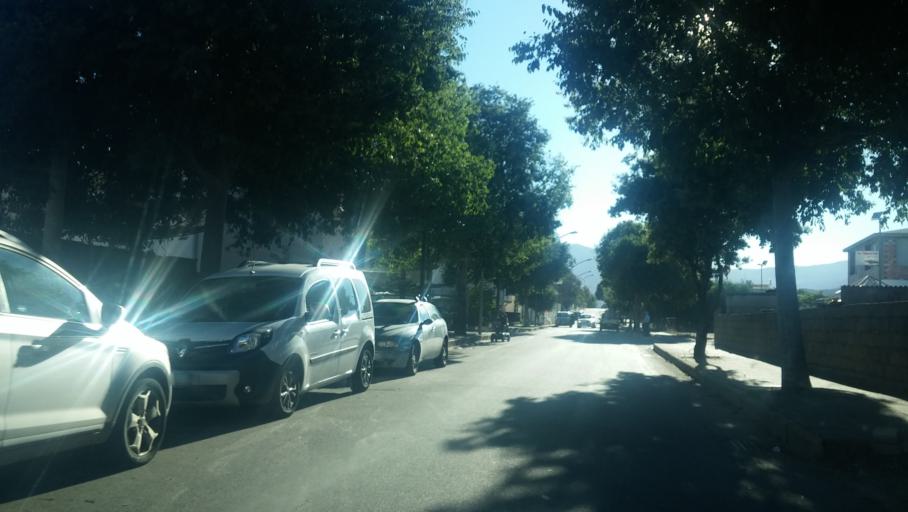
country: IT
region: Sardinia
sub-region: Provincia di Ogliastra
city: Lotzorai
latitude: 39.9691
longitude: 9.6596
